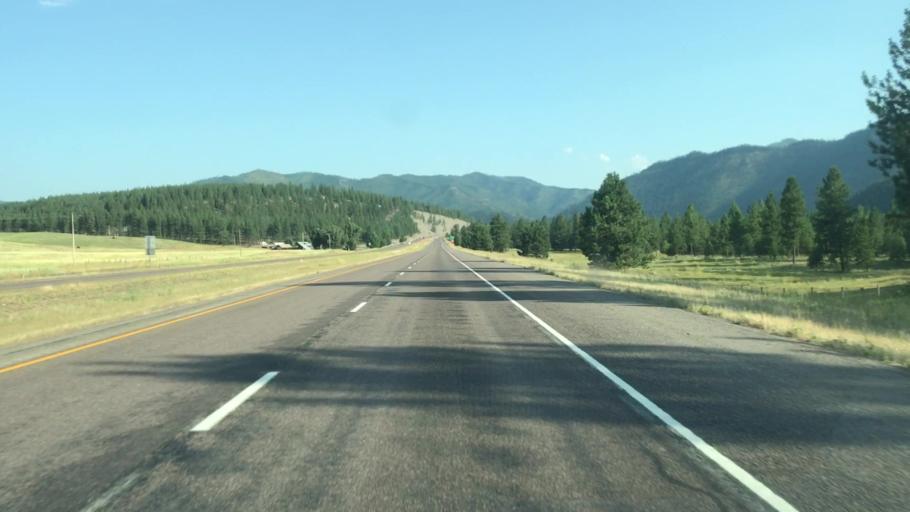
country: US
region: Montana
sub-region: Mineral County
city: Superior
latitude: 47.0338
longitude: -114.7448
